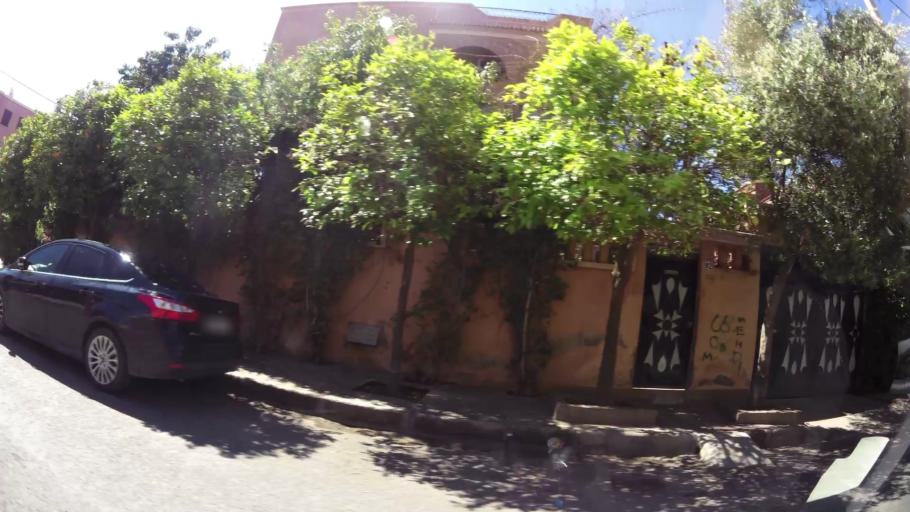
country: MA
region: Marrakech-Tensift-Al Haouz
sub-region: Marrakech
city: Marrakesh
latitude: 31.6377
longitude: -8.0625
